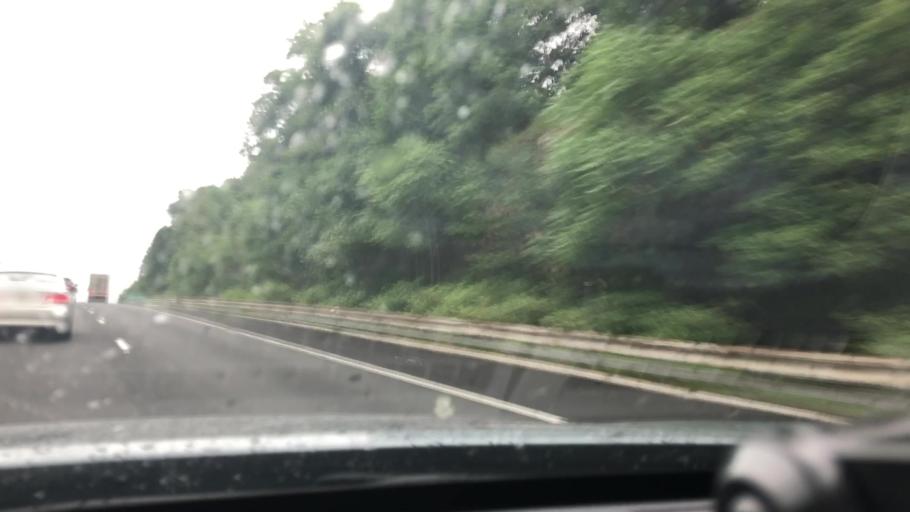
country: US
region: New Jersey
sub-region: Essex County
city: Essex Fells
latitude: 40.8007
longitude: -74.2760
